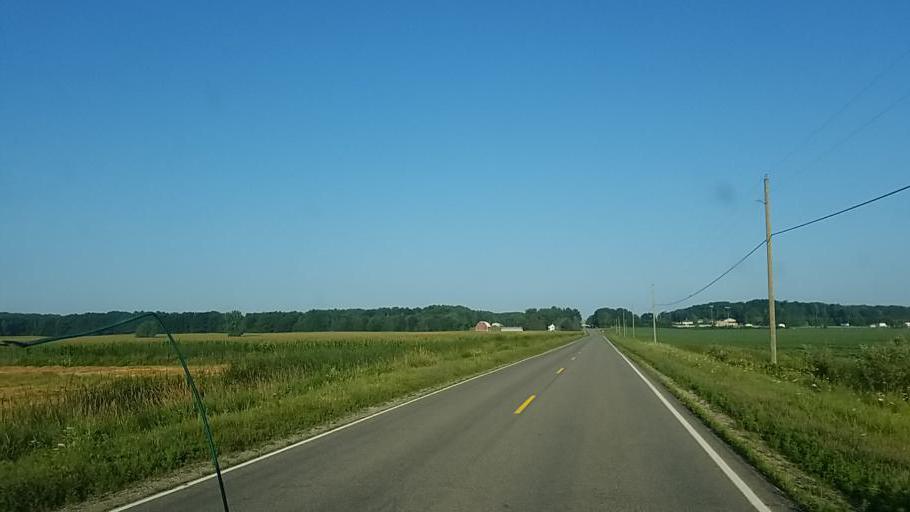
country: US
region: Michigan
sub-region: Montcalm County
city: Howard City
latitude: 43.3667
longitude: -85.4966
